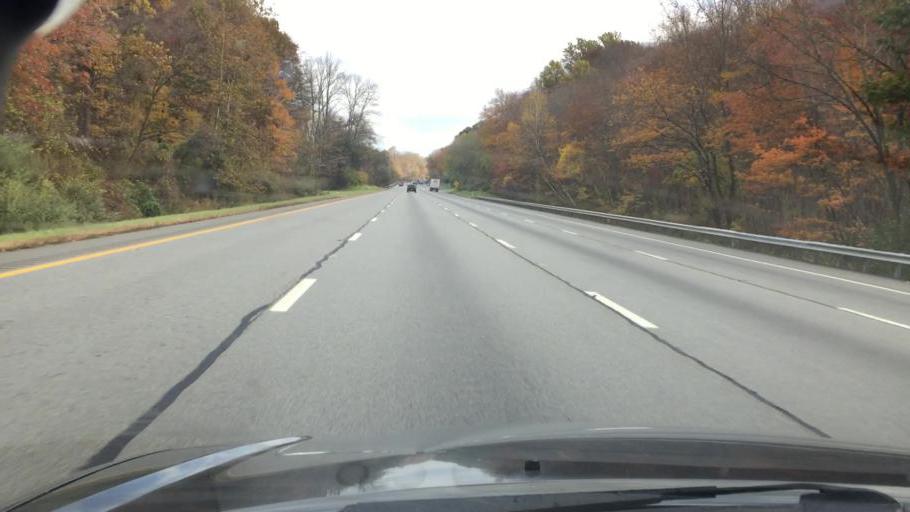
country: US
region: New Jersey
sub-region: Warren County
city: Hackettstown
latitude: 40.9283
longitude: -74.9115
